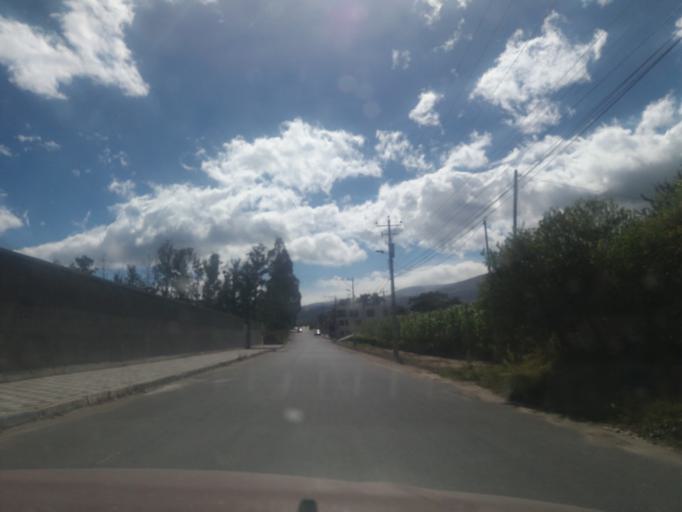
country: EC
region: Pichincha
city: Quito
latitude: -0.1699
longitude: -78.3392
